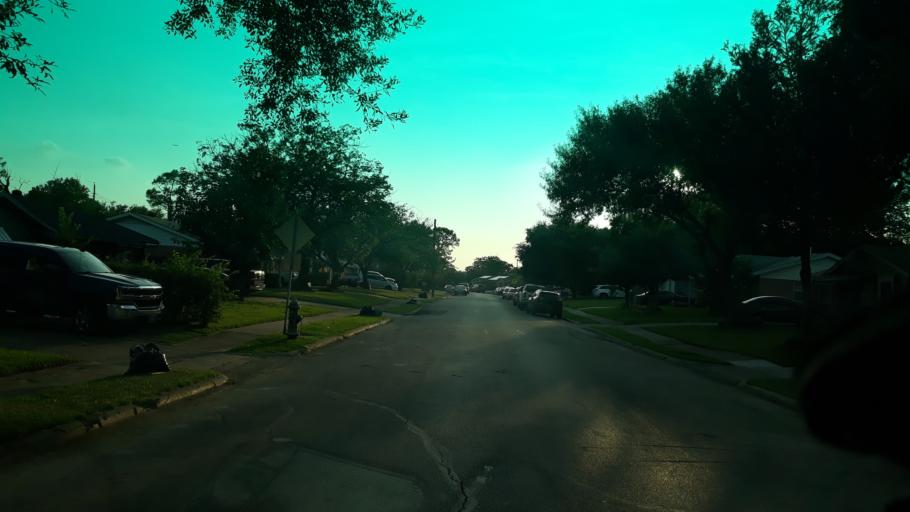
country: US
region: Texas
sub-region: Dallas County
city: Irving
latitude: 32.8437
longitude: -96.9799
